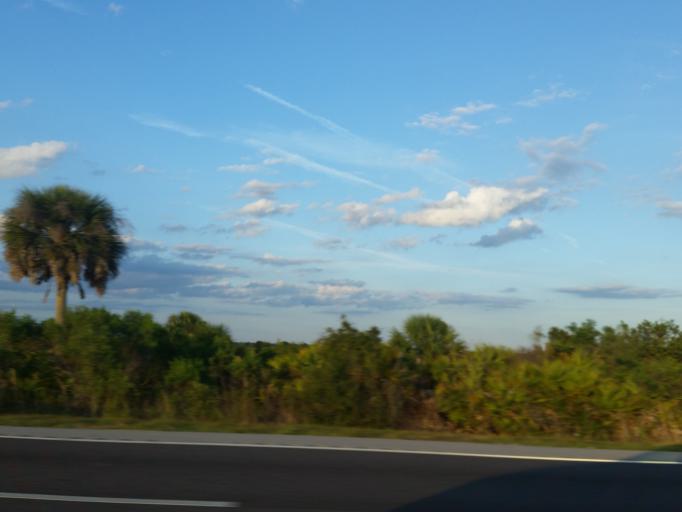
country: US
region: Florida
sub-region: Sarasota County
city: Laurel
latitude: 27.1903
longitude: -82.4378
